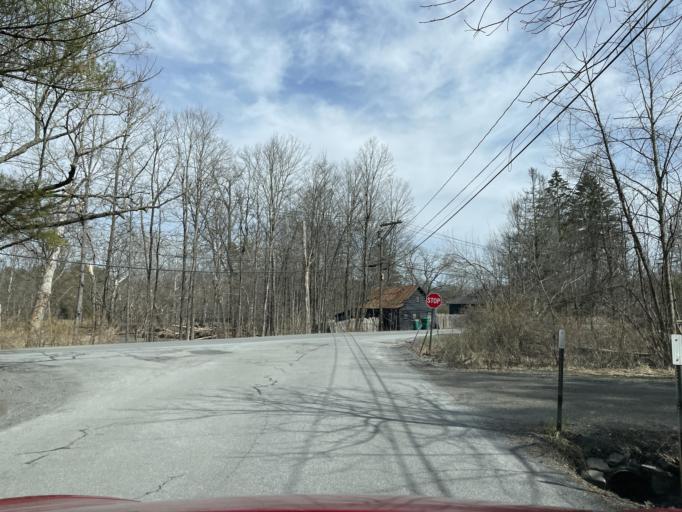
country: US
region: New York
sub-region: Ulster County
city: Zena
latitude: 42.0178
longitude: -74.0777
